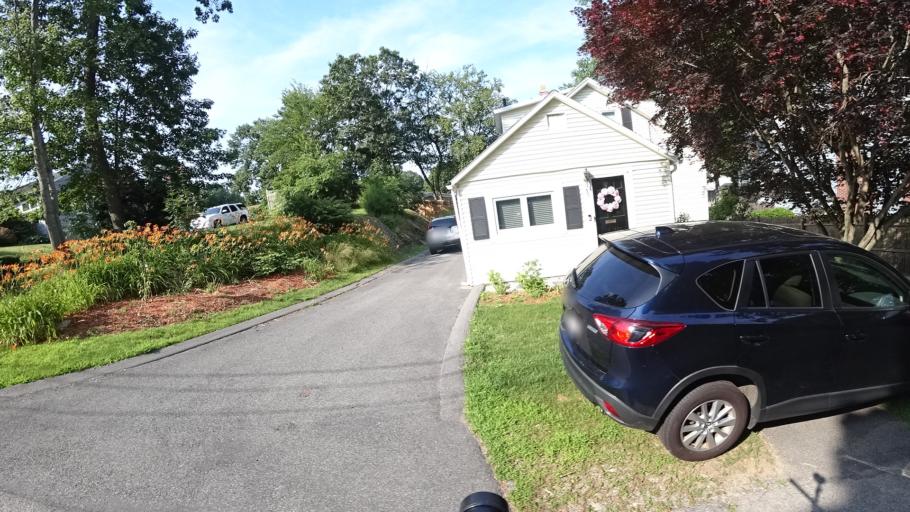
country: US
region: Massachusetts
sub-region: Norfolk County
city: Dedham
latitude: 42.2302
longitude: -71.1586
